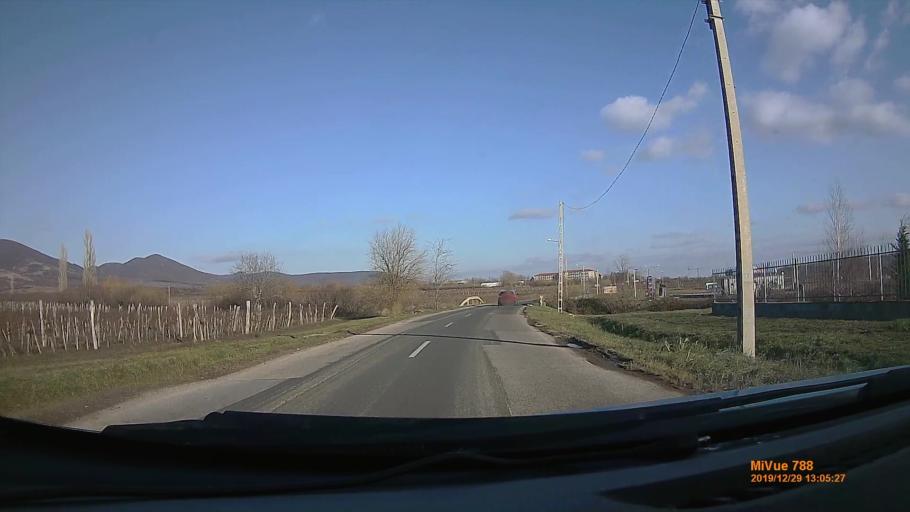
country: HU
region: Heves
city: Abasar
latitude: 47.8052
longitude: 20.0140
